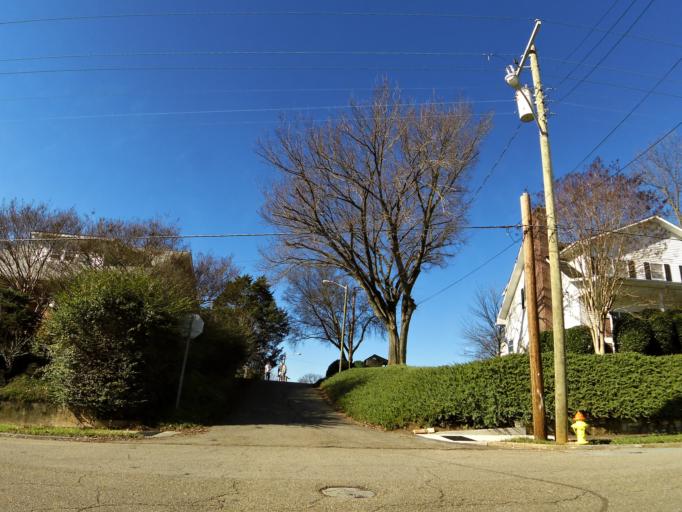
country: US
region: Tennessee
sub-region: Knox County
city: Knoxville
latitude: 35.9706
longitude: -83.9395
